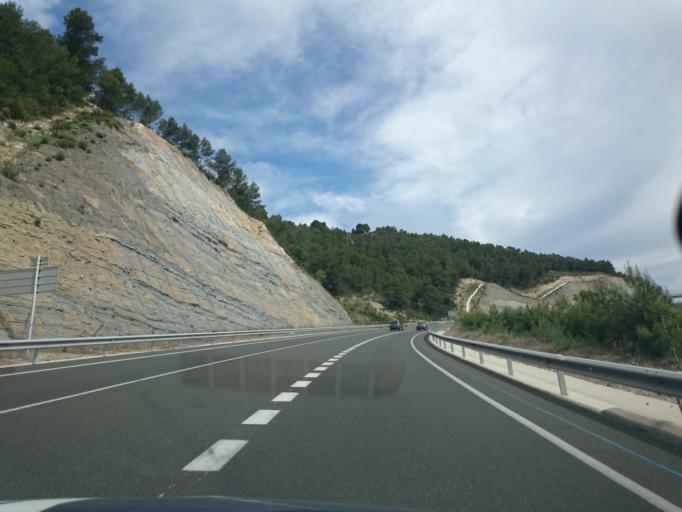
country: ES
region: Catalonia
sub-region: Provincia de Barcelona
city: Castelloli
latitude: 41.6158
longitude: 1.6808
